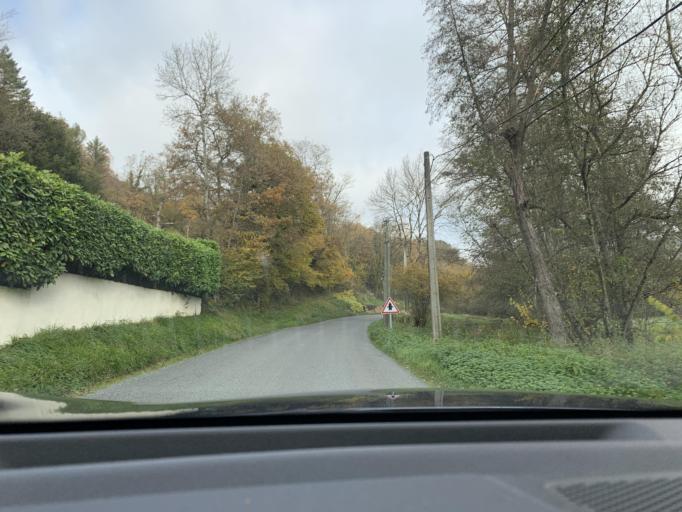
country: FR
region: Rhone-Alpes
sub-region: Departement du Rhone
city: Chessy
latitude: 45.8881
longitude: 4.6433
